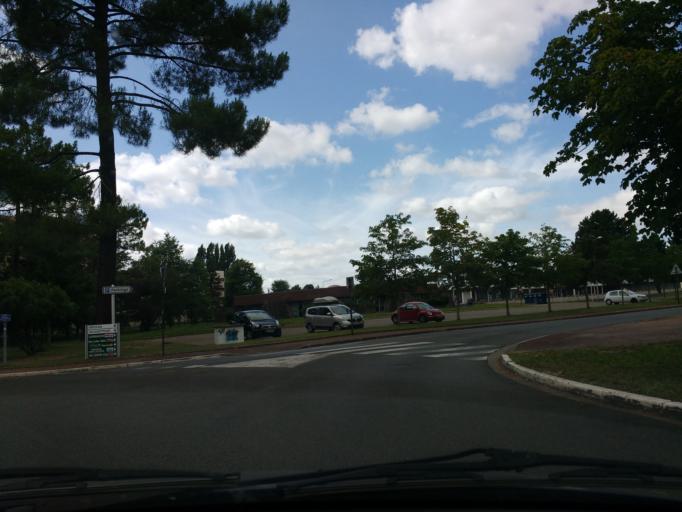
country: FR
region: Aquitaine
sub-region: Departement de la Gironde
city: Gradignan
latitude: 44.7710
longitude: -0.6095
